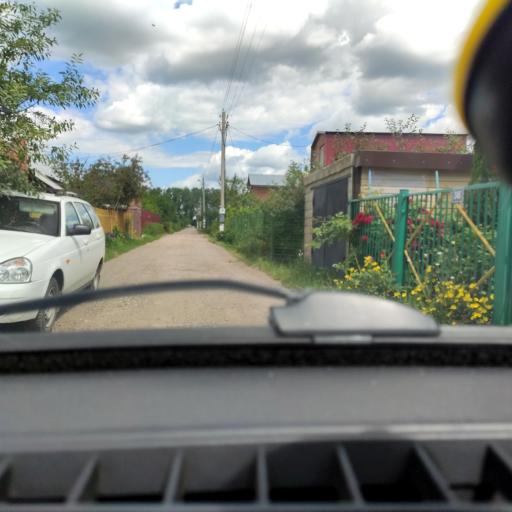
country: RU
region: Samara
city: Podstepki
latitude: 53.6042
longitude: 49.2261
